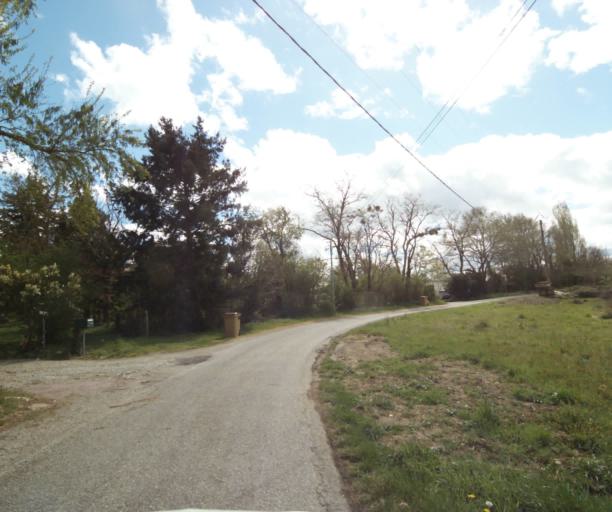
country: FR
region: Midi-Pyrenees
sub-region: Departement de l'Ariege
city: Saverdun
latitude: 43.2607
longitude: 1.5976
